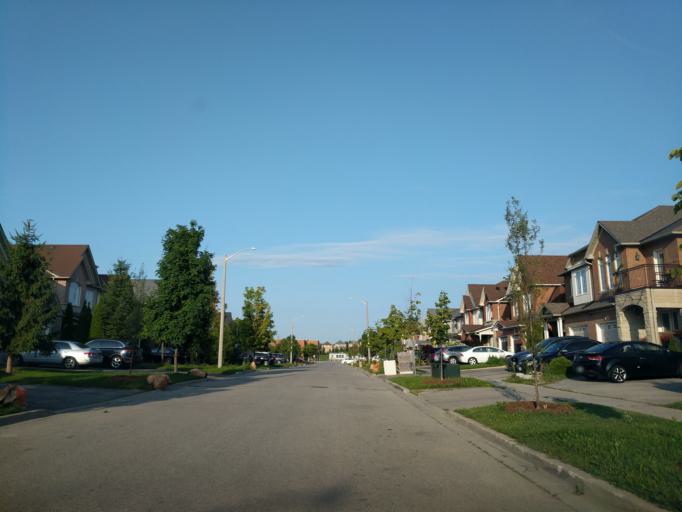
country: CA
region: Ontario
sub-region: York
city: Richmond Hill
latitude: 43.9037
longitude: -79.4545
